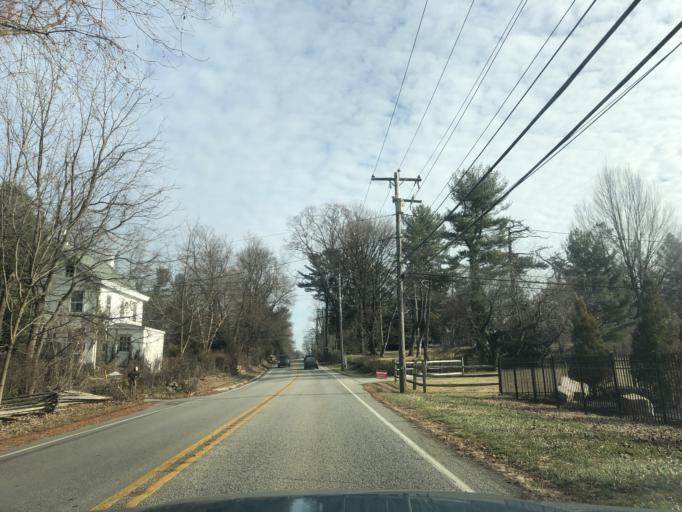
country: US
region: Pennsylvania
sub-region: Delaware County
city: Radnor
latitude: 40.0264
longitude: -75.3471
